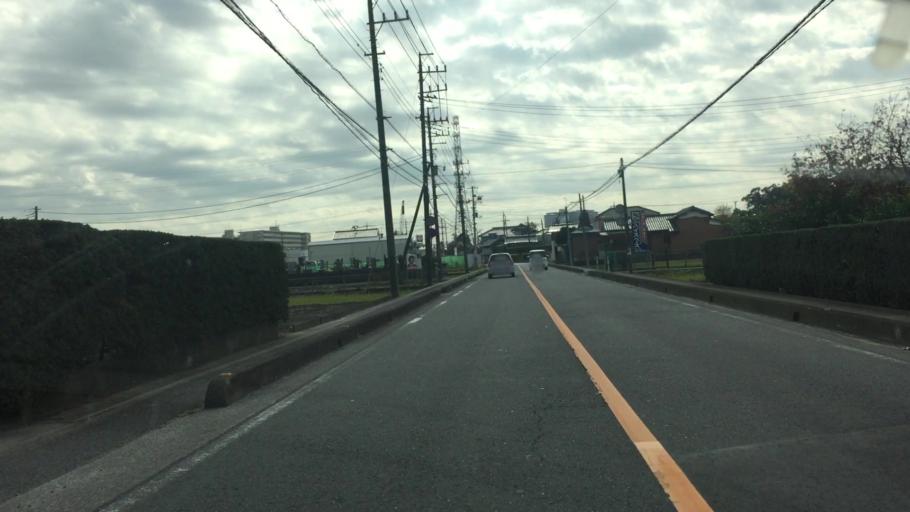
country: JP
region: Saitama
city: Yoshikawa
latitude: 35.8691
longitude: 139.8654
